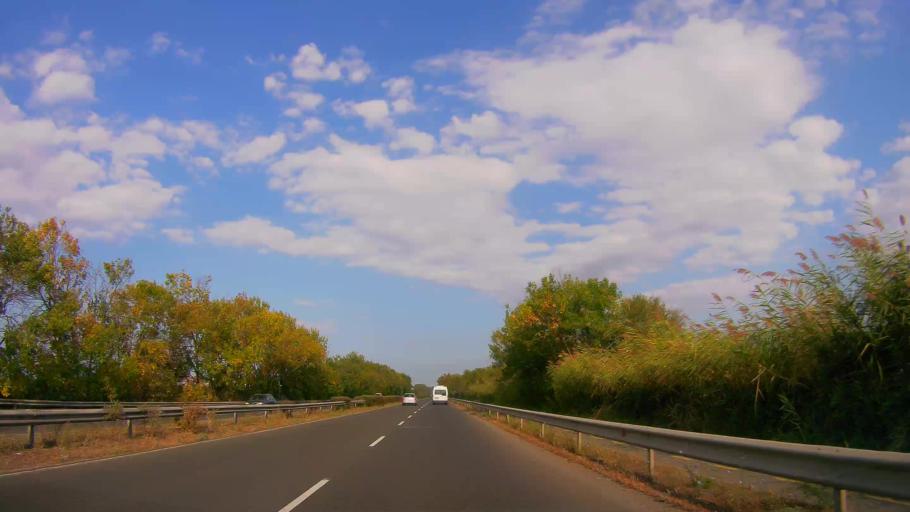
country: BG
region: Burgas
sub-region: Obshtina Burgas
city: Burgas
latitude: 42.4476
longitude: 27.4566
